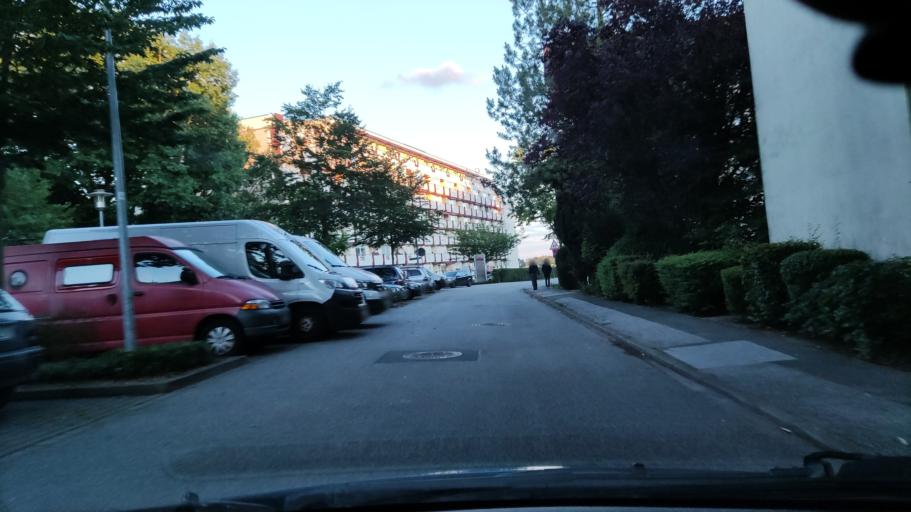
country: DE
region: Schleswig-Holstein
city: Wedel
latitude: 53.5689
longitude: 9.7137
